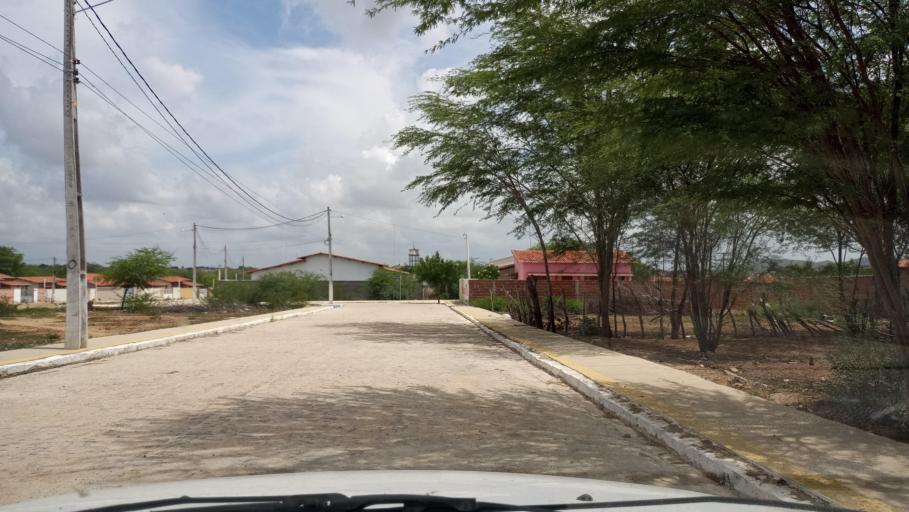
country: BR
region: Rio Grande do Norte
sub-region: Tangara
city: Tangara
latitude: -6.1112
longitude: -35.7153
